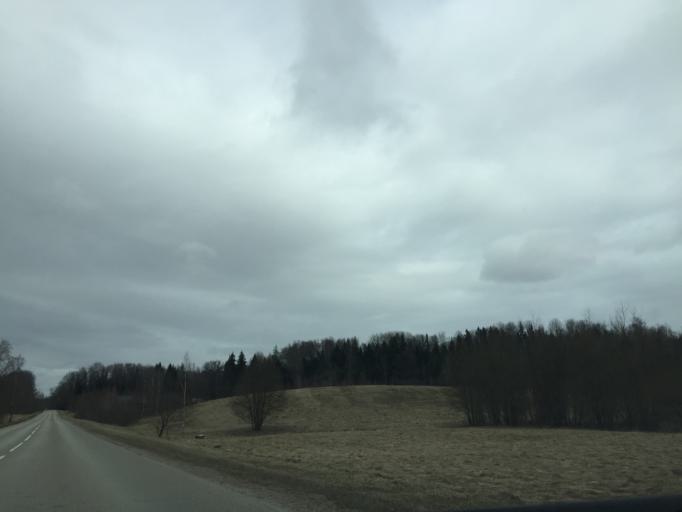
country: LV
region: Kraslavas Rajons
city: Kraslava
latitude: 55.9453
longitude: 27.1626
